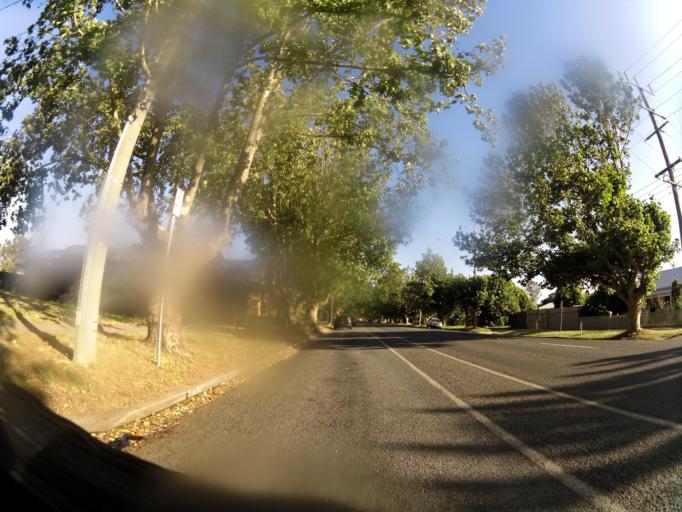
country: AU
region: Victoria
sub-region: Murrindindi
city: Kinglake West
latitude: -37.0227
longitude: 145.1319
